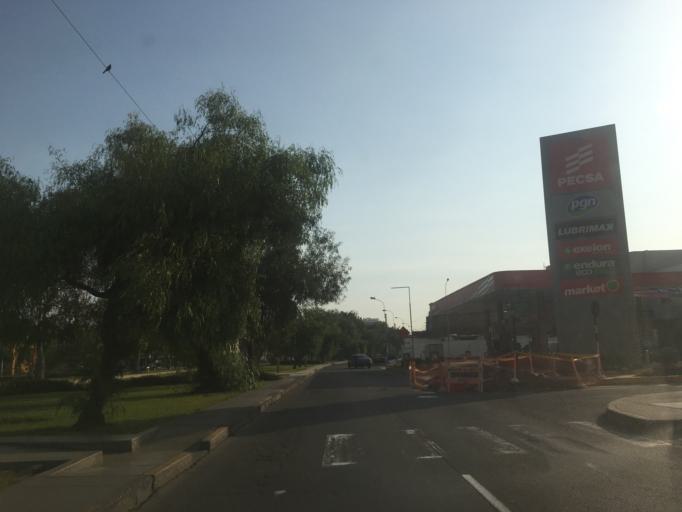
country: PE
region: Lima
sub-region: Lima
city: La Molina
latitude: -12.0677
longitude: -76.9461
